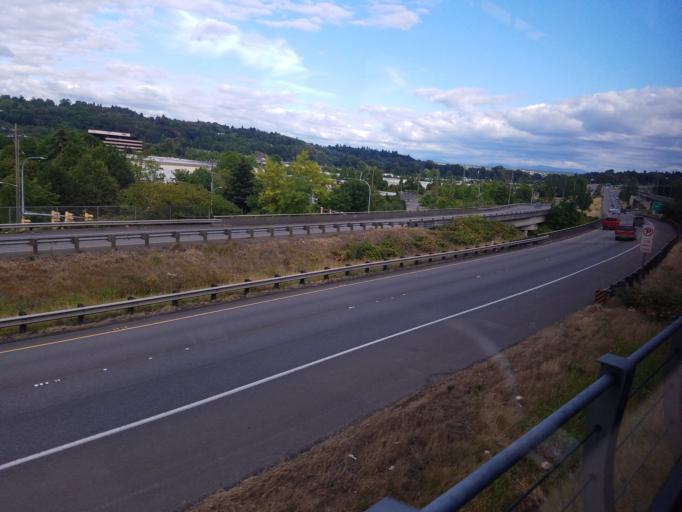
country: US
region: Washington
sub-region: King County
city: Riverton
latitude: 47.4895
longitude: -122.2813
